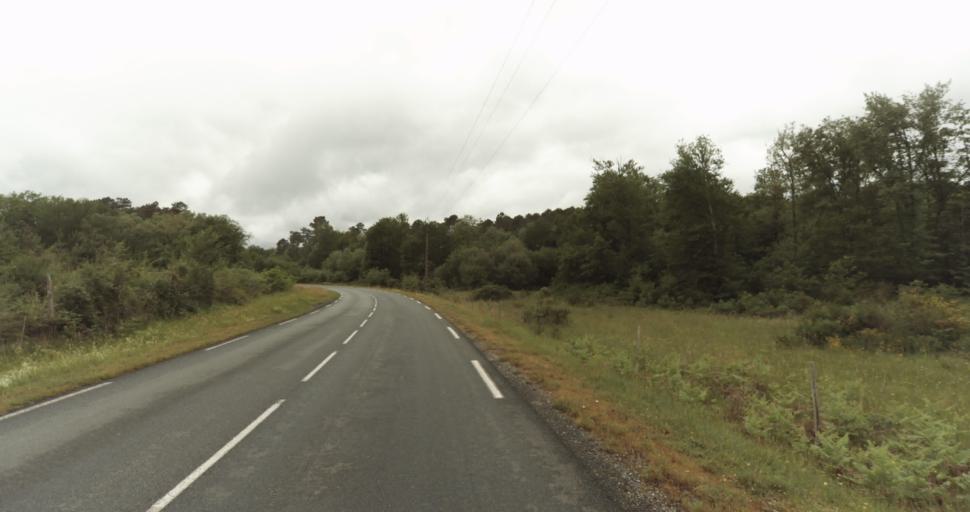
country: FR
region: Aquitaine
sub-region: Departement de la Dordogne
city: Belves
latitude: 44.6874
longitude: 0.9863
